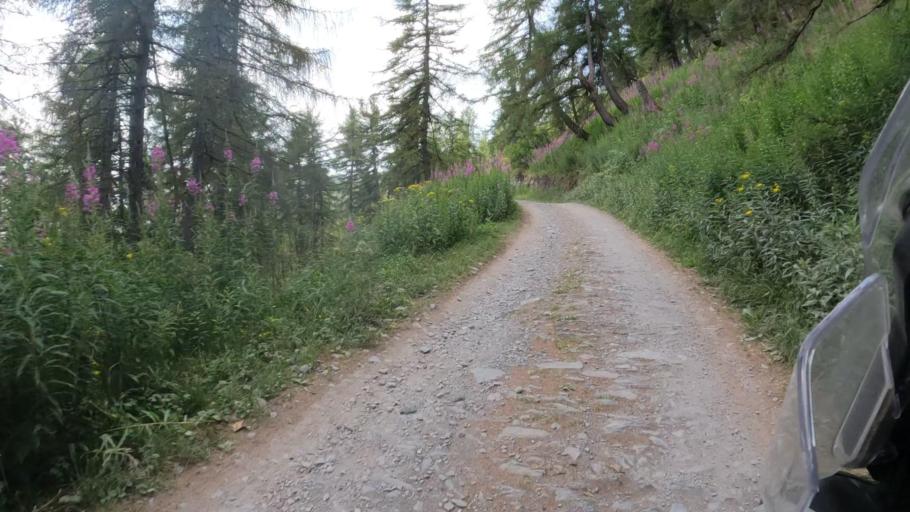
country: IT
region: Liguria
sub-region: Provincia di Imperia
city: Pigna
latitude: 44.0211
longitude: 7.6647
